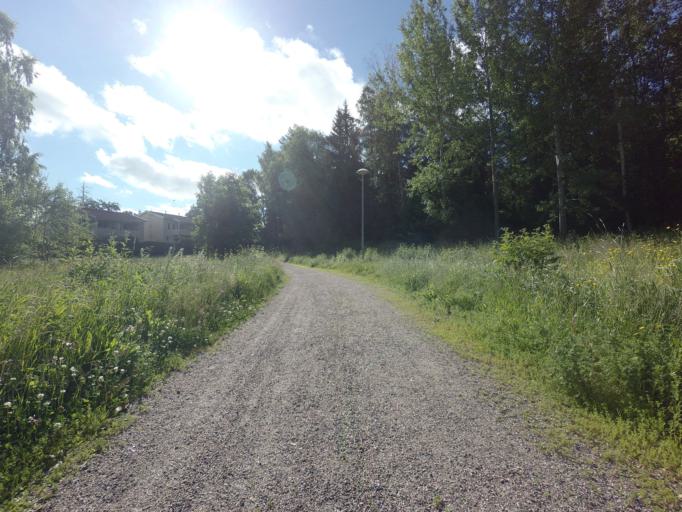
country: FI
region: Uusimaa
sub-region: Helsinki
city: Espoo
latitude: 60.1722
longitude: 24.6916
